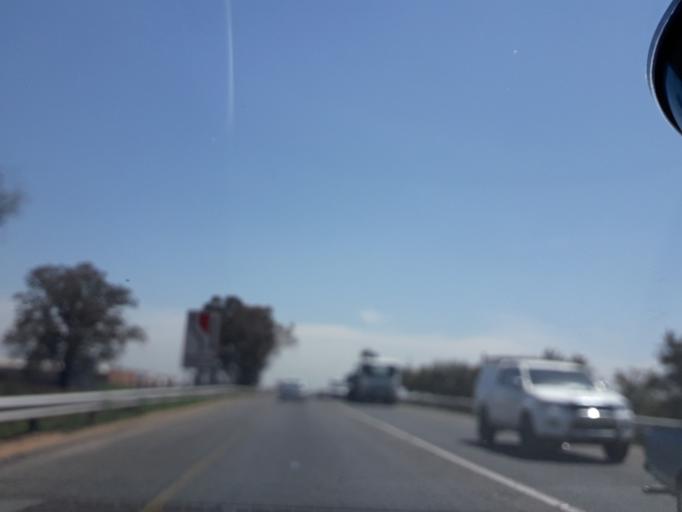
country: ZA
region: Gauteng
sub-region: City of Tshwane Metropolitan Municipality
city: Centurion
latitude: -25.8829
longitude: 28.1613
